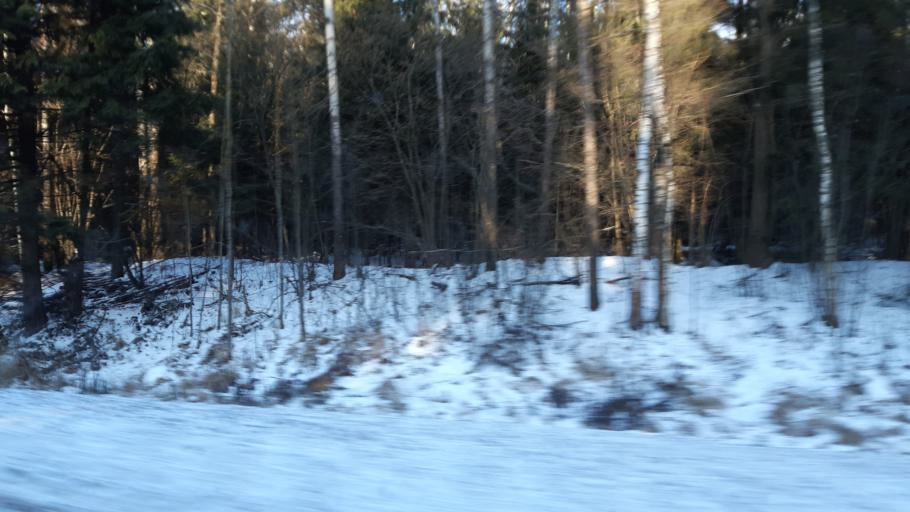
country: RU
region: Vladimir
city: Arsaki
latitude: 56.2944
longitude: 38.3704
